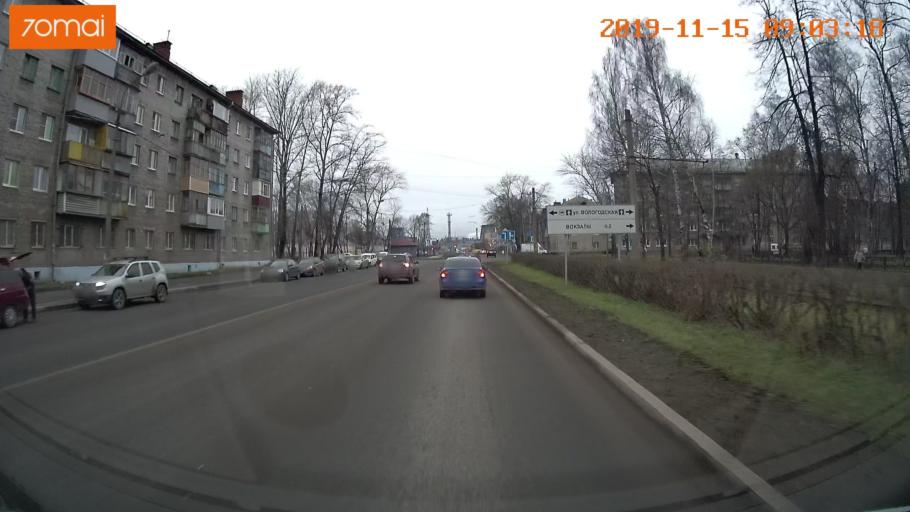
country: RU
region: Vologda
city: Cherepovets
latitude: 59.1381
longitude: 37.9226
